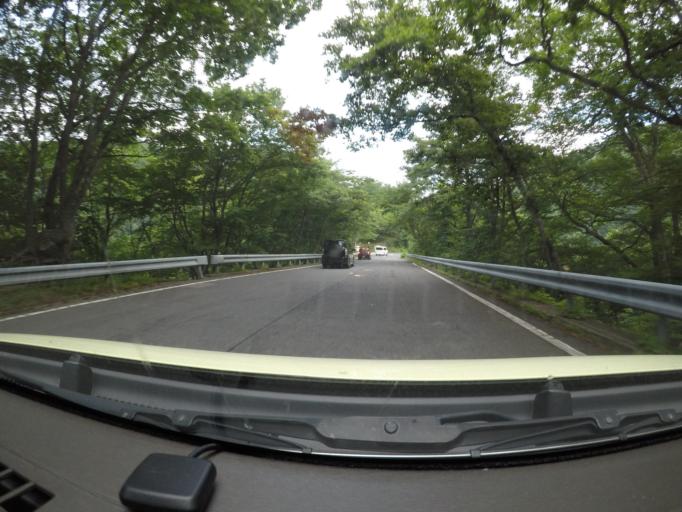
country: JP
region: Tochigi
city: Nikko
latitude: 36.7444
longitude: 139.5147
